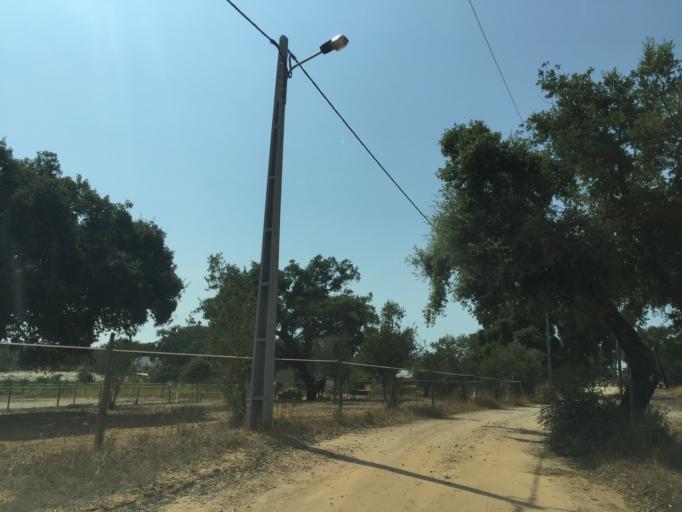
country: PT
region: Setubal
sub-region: Grandola
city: Grandola
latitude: 38.0046
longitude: -8.4942
